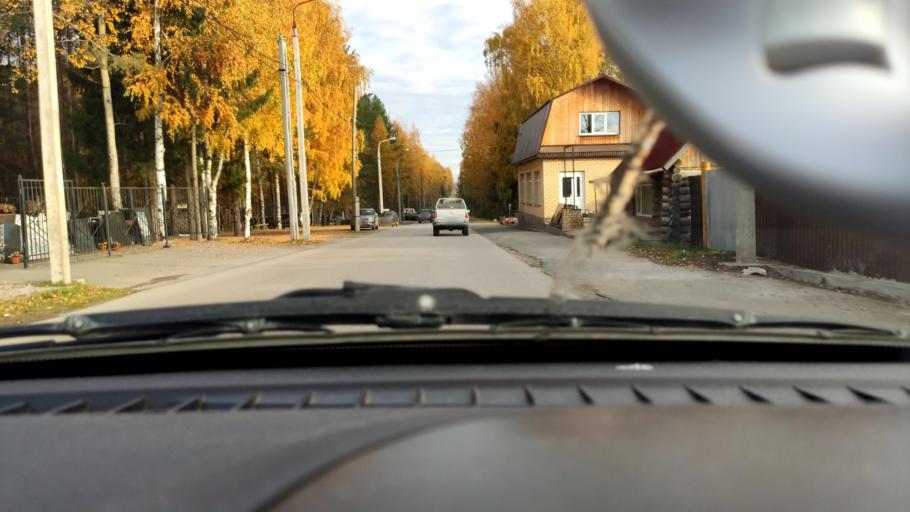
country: RU
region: Perm
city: Kondratovo
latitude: 58.0597
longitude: 56.1242
